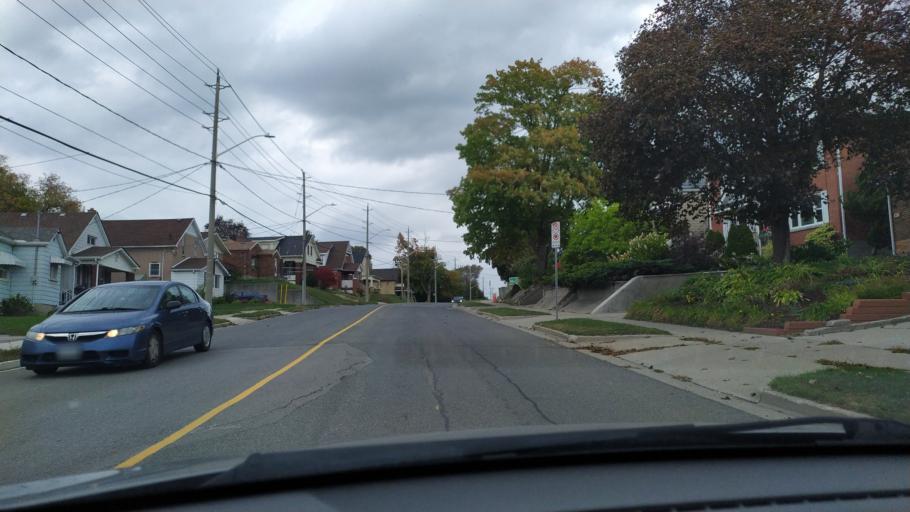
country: CA
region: Ontario
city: Waterloo
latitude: 43.4629
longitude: -80.4839
